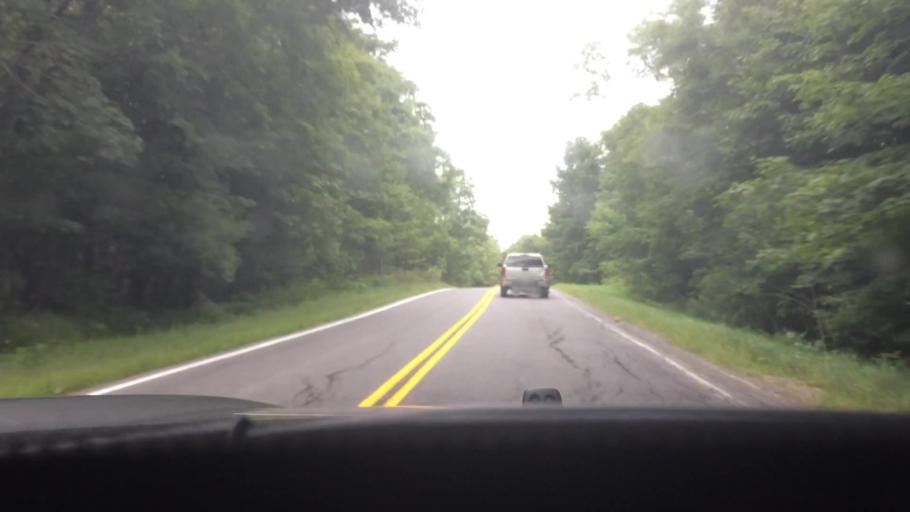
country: US
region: New York
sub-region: St. Lawrence County
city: Canton
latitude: 44.5322
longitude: -75.1799
